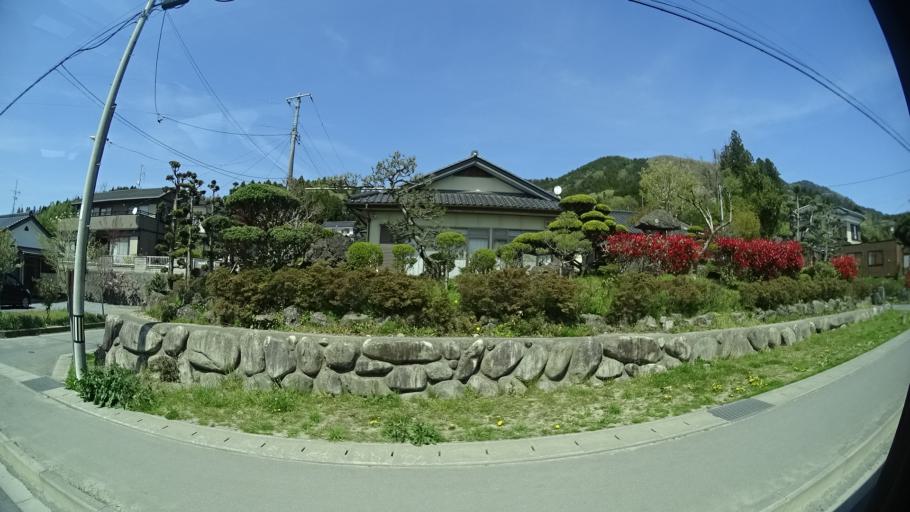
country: JP
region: Iwate
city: Ofunato
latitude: 39.0117
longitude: 141.6725
